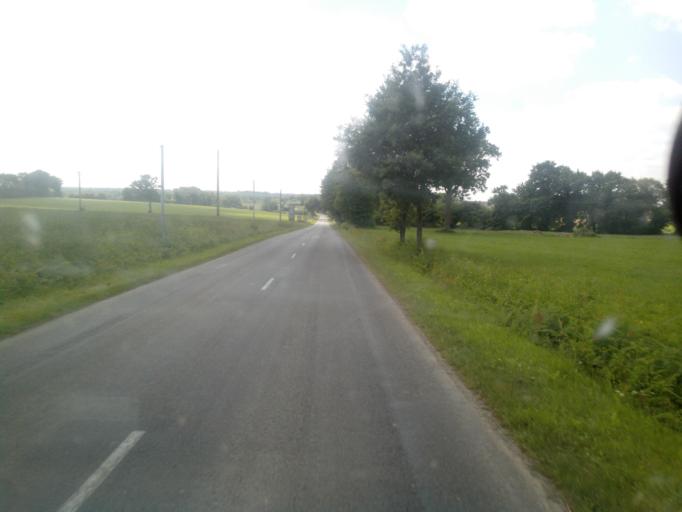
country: FR
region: Brittany
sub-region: Departement d'Ille-et-Vilaine
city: Sens-de-Bretagne
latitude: 48.3276
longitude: -1.5728
